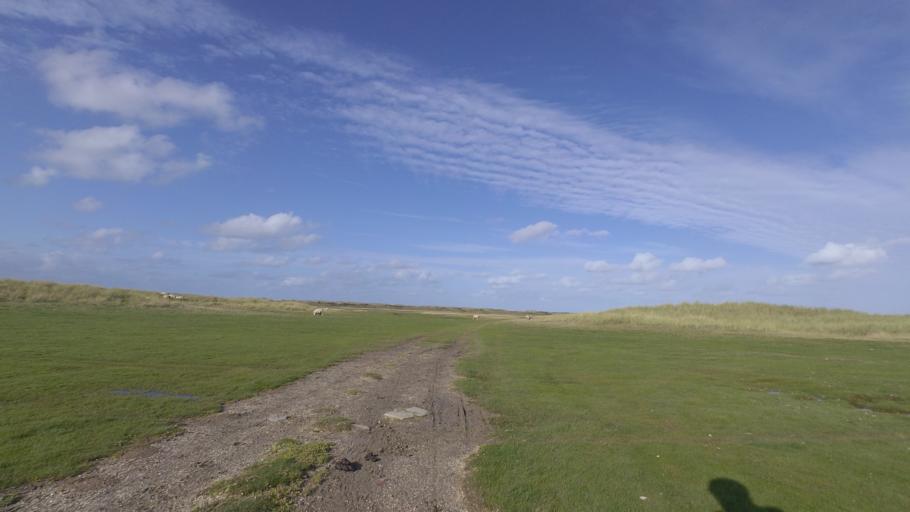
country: NL
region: Friesland
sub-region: Gemeente Ameland
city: Nes
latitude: 53.4548
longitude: 5.8637
